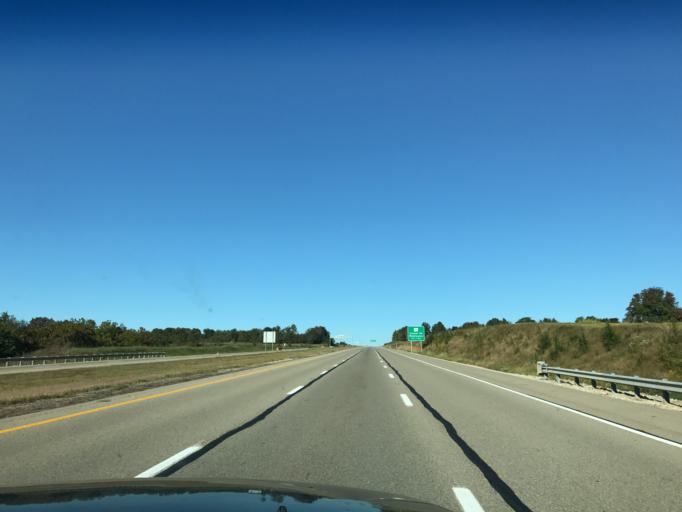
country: US
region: West Virginia
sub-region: Wood County
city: Blennerhassett
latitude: 39.2569
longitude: -81.6288
